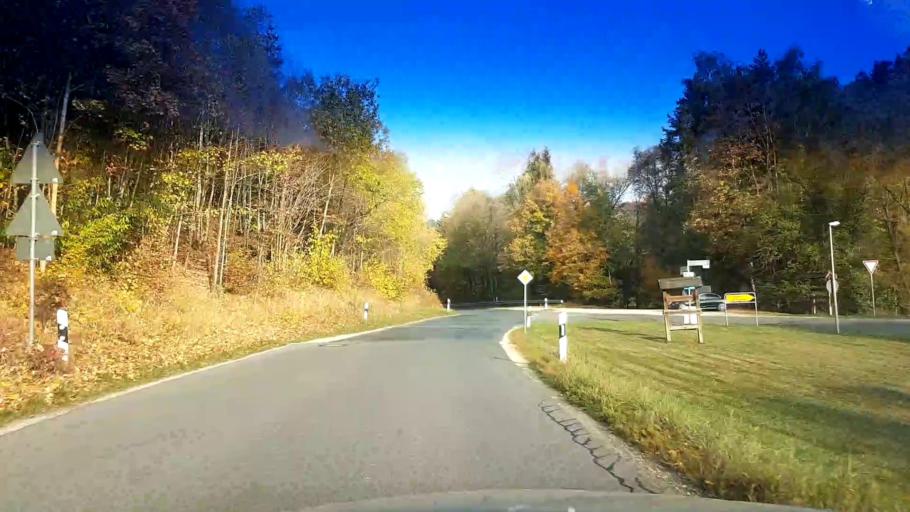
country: DE
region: Bavaria
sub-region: Upper Franconia
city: Stadelhofen
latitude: 50.0225
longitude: 11.1987
